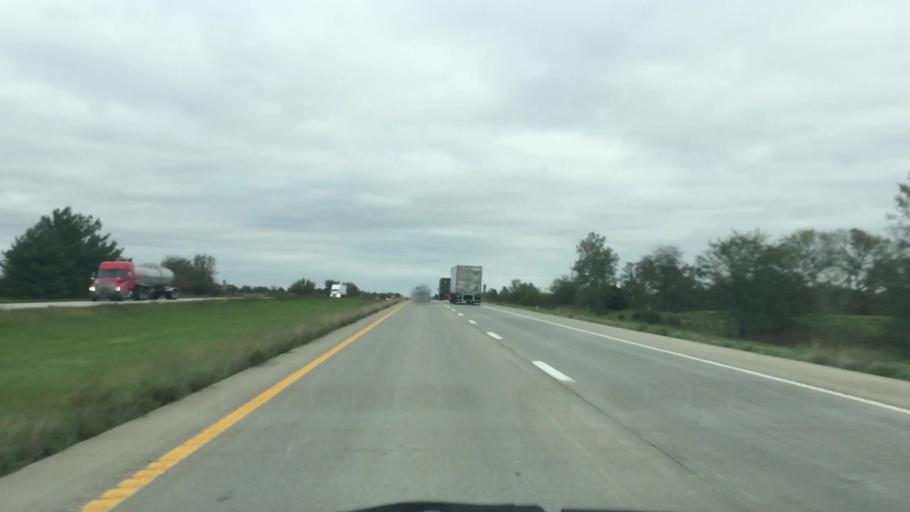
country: US
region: Missouri
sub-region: Clinton County
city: Lathrop
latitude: 39.6124
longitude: -94.2501
